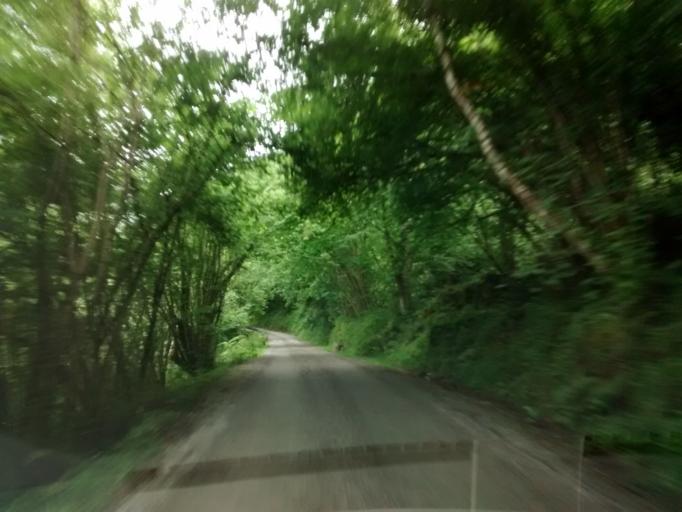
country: ES
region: Asturias
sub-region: Province of Asturias
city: Pilona
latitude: 43.2730
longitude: -5.3477
